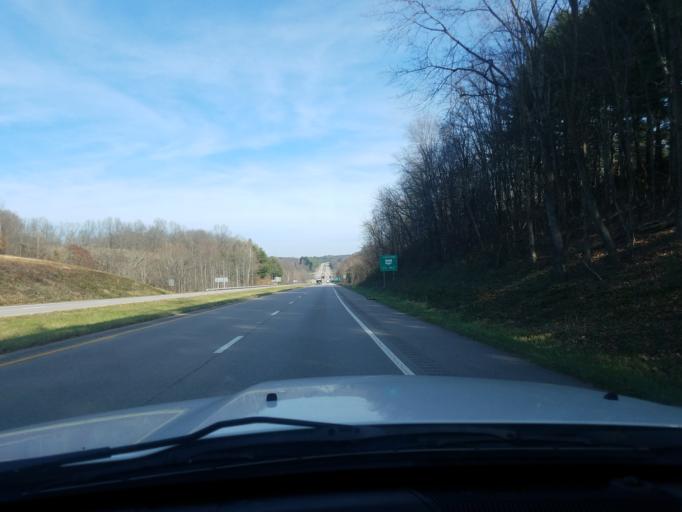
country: US
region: West Virginia
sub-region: Wood County
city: Washington
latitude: 39.2216
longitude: -81.8037
